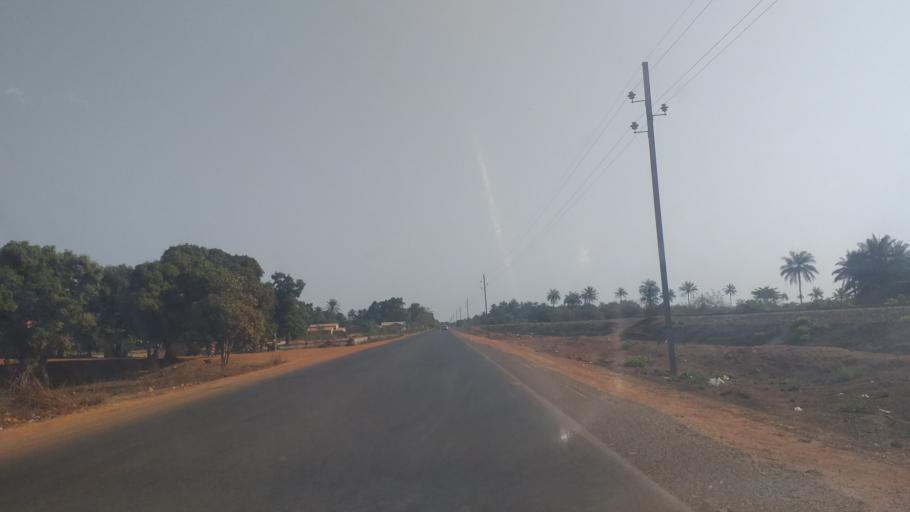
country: GN
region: Boke
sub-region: Boke Prefecture
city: Kamsar
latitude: 10.7201
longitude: -14.5207
